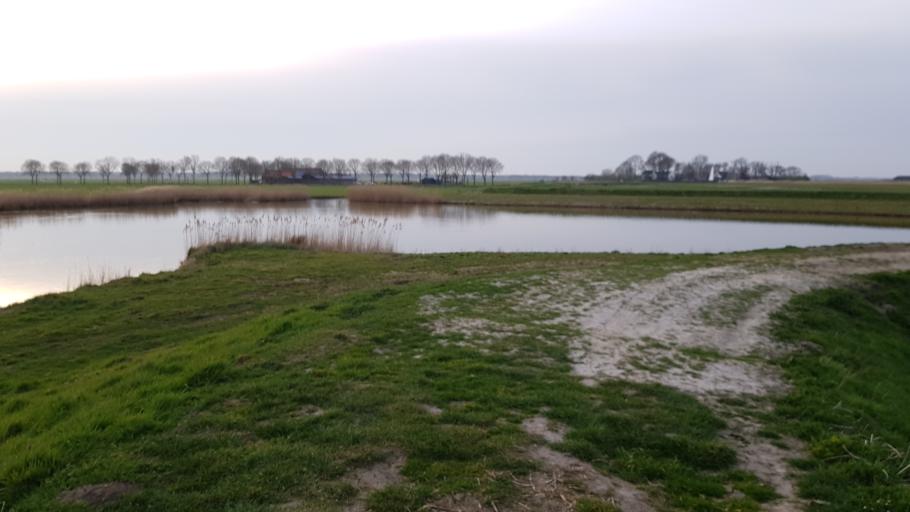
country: NL
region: Utrecht
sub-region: Gemeente Baarn
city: Baarn
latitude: 52.2434
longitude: 5.3077
